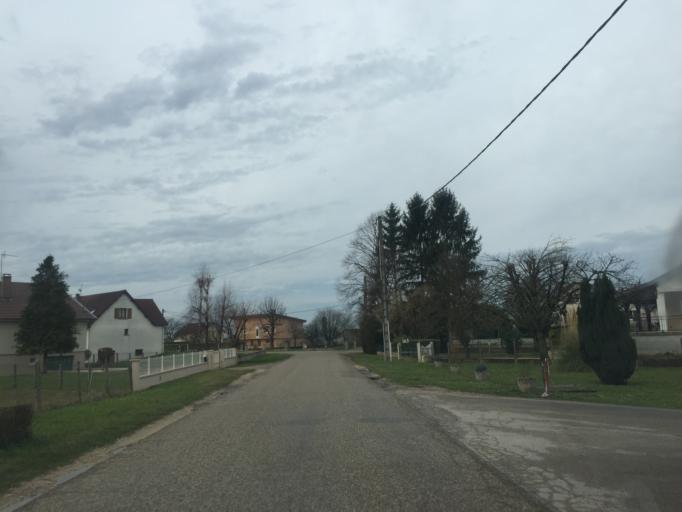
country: FR
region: Franche-Comte
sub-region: Departement du Jura
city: Choisey
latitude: 47.0377
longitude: 5.4387
